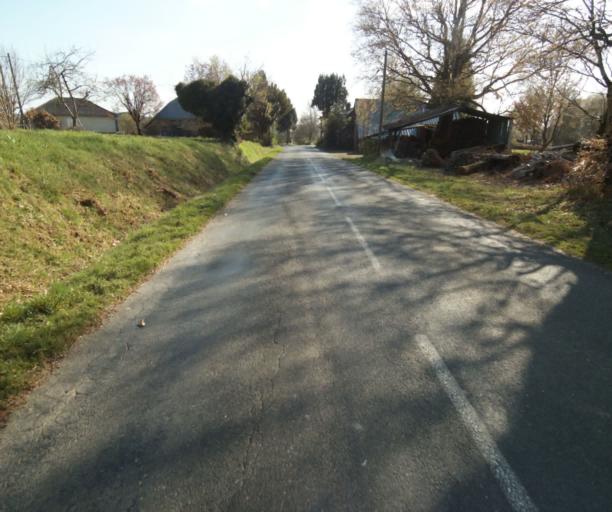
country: FR
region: Limousin
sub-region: Departement de la Correze
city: Saint-Mexant
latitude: 45.3330
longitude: 1.6104
